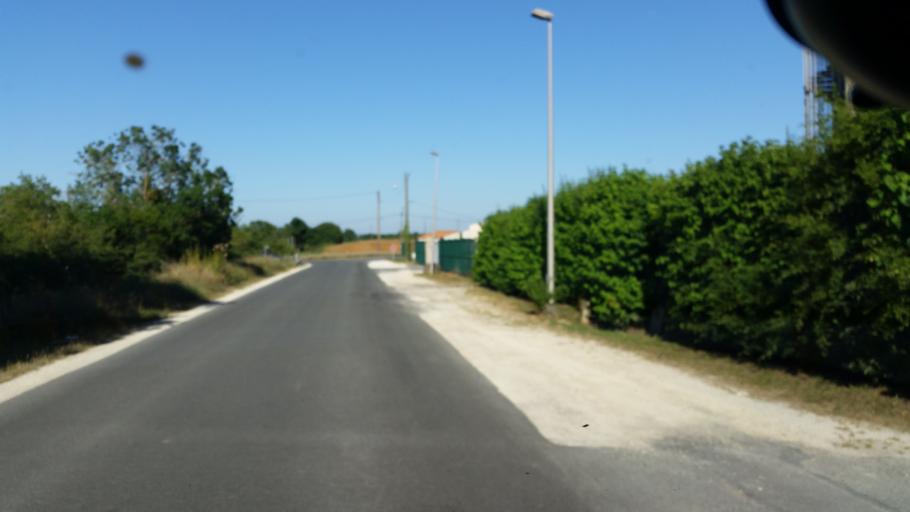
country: FR
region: Poitou-Charentes
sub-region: Departement de la Charente-Maritime
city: Marans
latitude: 46.3019
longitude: -0.9847
